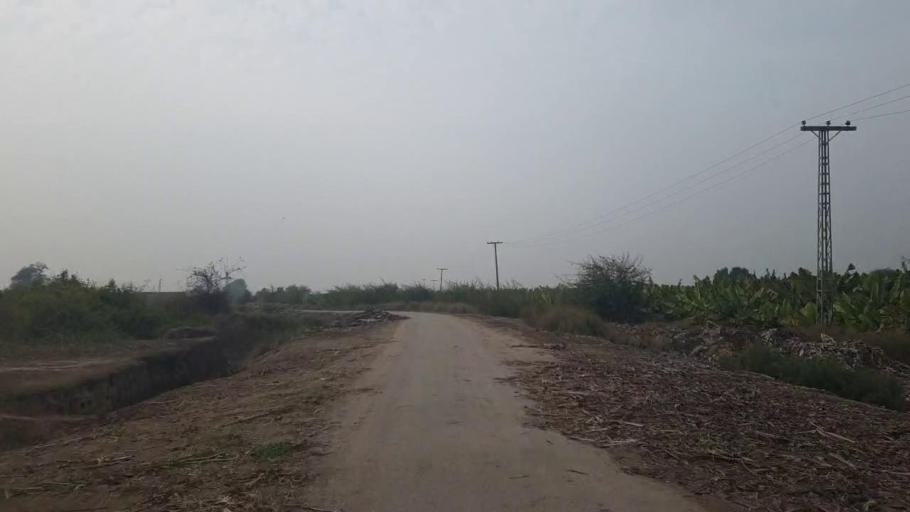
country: PK
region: Sindh
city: Tando Adam
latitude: 25.8240
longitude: 68.7081
